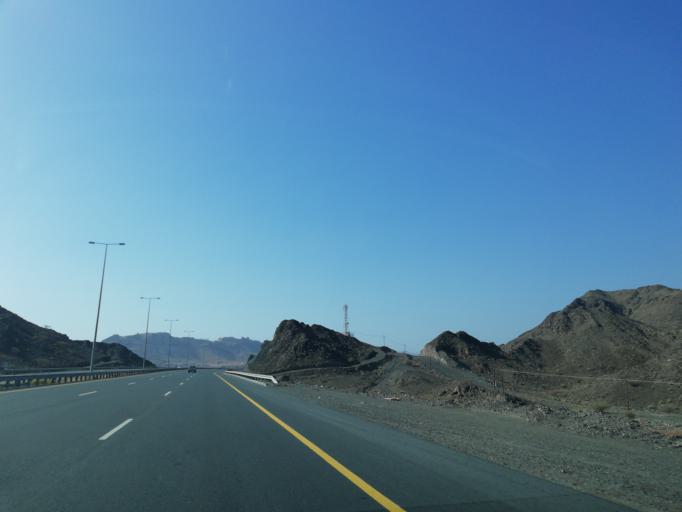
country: OM
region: Ash Sharqiyah
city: Ibra'
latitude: 22.9679
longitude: 58.2425
